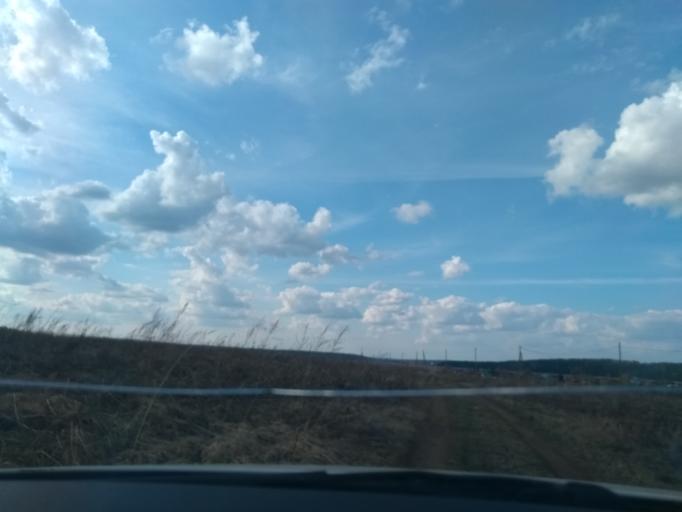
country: RU
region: Perm
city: Sylva
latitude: 57.8423
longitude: 56.7909
